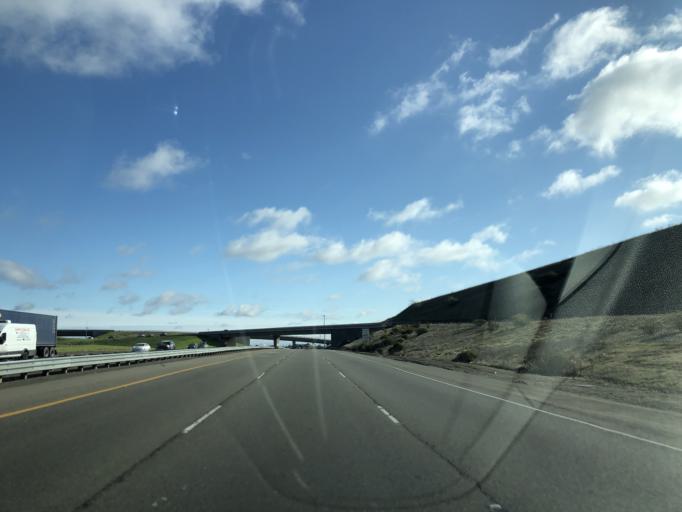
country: US
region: California
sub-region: Contra Costa County
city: Antioch
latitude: 37.9910
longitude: -121.7621
